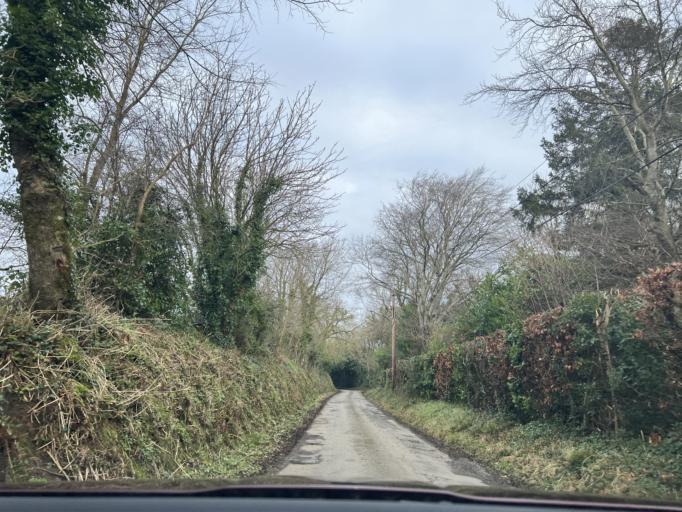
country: IE
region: Leinster
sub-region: Loch Garman
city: Loch Garman
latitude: 52.3730
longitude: -6.5402
